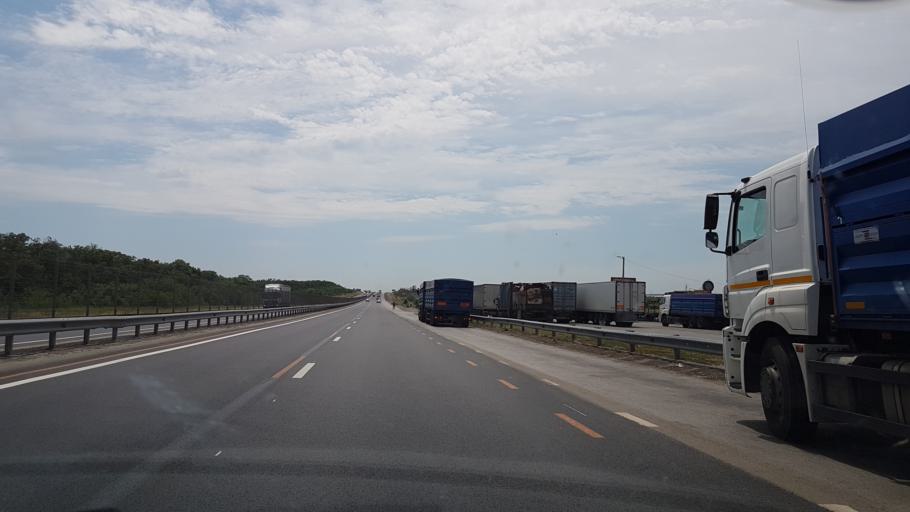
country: RU
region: Rostov
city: Likhoy
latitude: 48.0987
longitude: 40.2595
